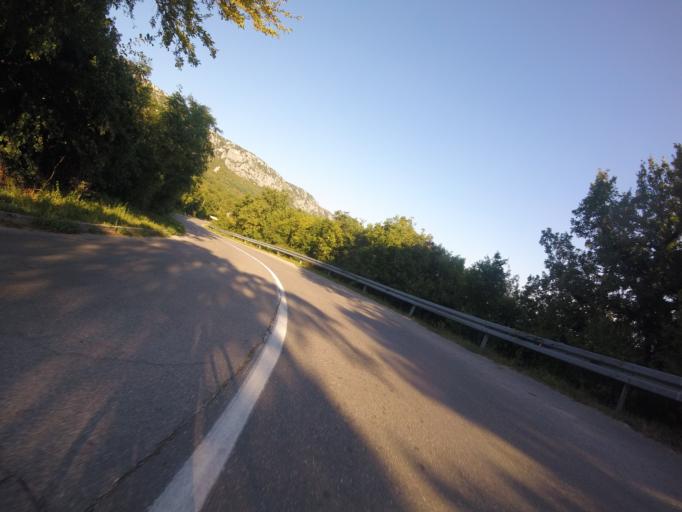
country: HR
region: Primorsko-Goranska
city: Bribir
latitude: 45.1699
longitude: 14.7481
